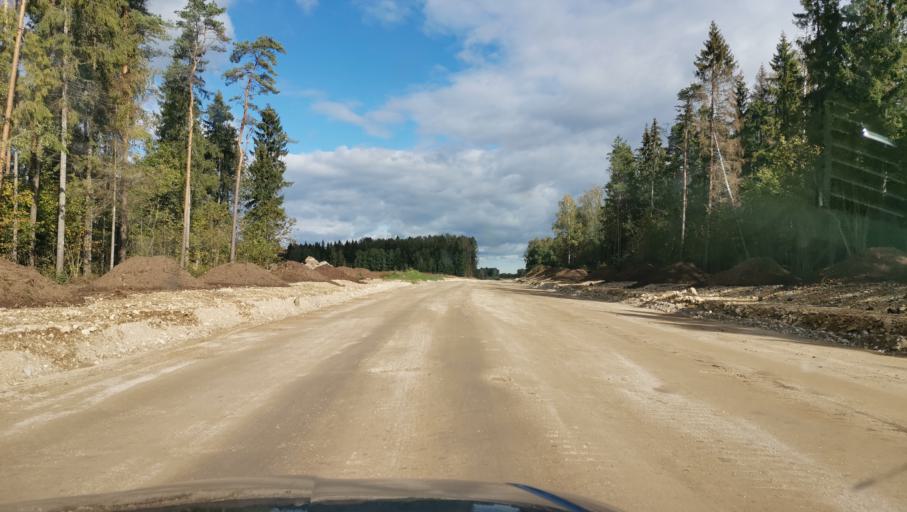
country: EE
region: Harju
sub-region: Nissi vald
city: Riisipere
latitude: 59.1362
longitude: 24.4838
